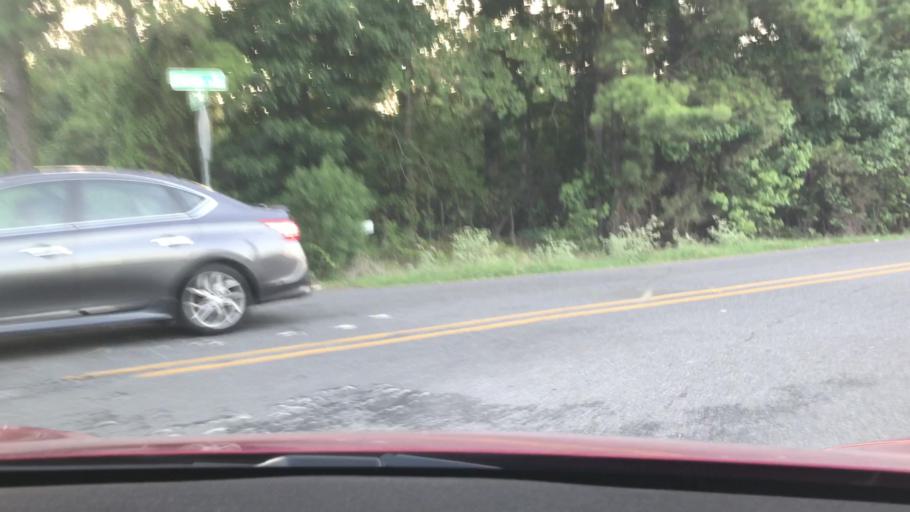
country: US
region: Louisiana
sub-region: Bossier Parish
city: Bossier City
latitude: 32.3910
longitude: -93.7548
